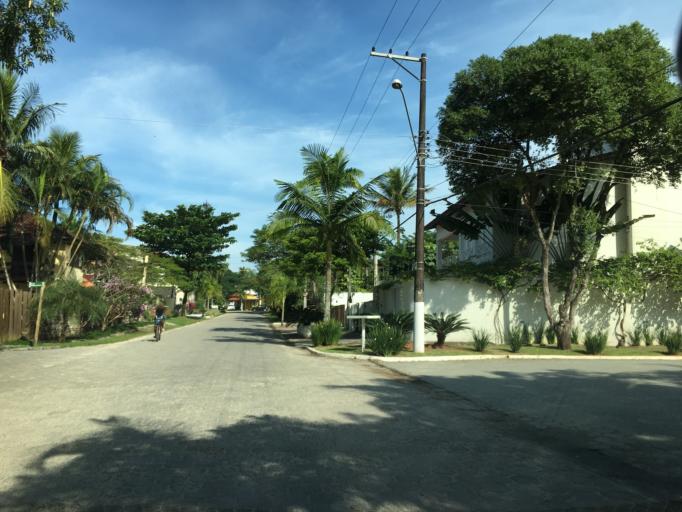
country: BR
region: Sao Paulo
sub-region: Sao Sebastiao
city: Sao Sebastiao
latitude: -23.7667
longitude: -45.7285
